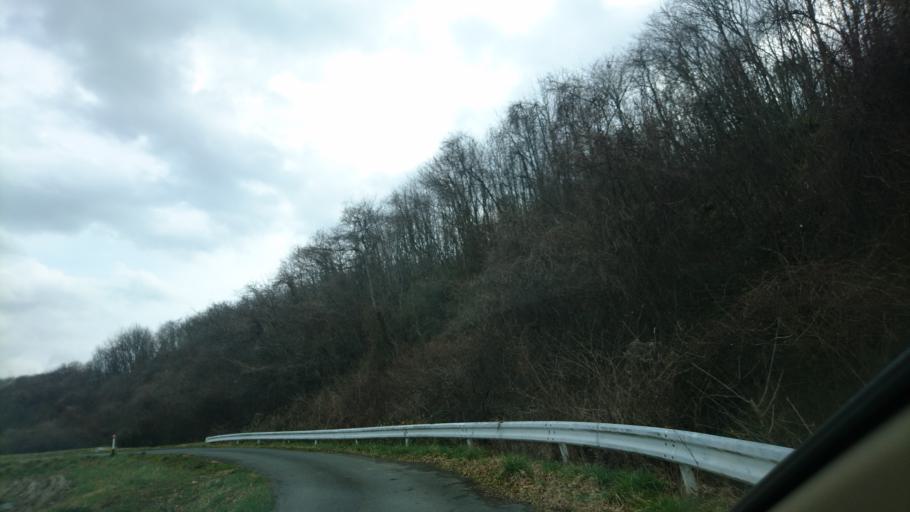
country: JP
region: Iwate
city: Ichinoseki
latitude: 38.8926
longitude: 141.1843
